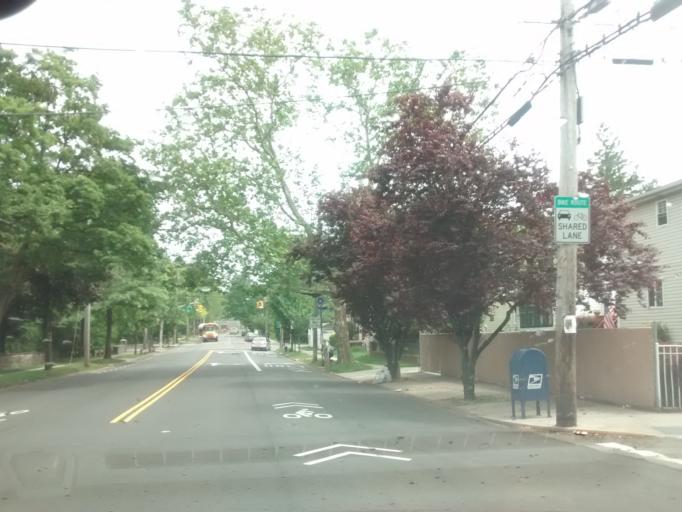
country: US
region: New York
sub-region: Kings County
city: Bensonhurst
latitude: 40.6079
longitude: -74.0616
